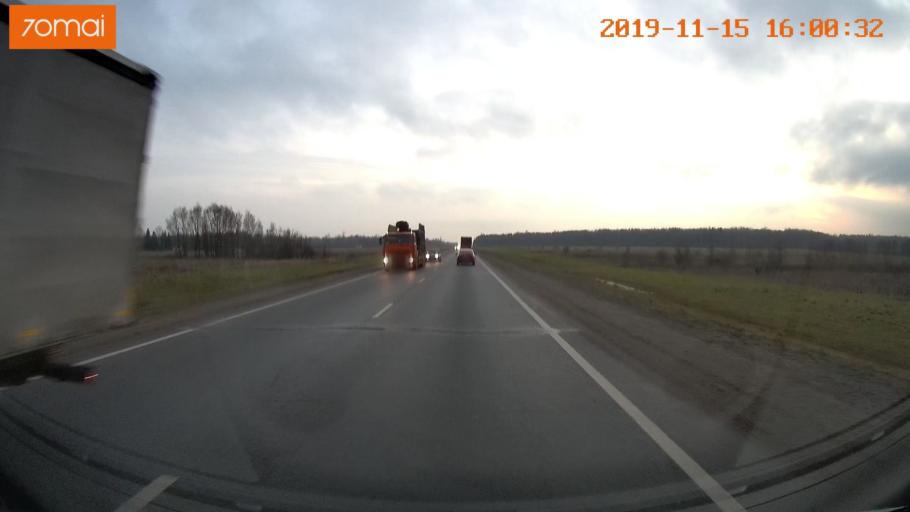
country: RU
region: Jaroslavl
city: Yaroslavl
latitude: 57.7948
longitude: 39.9382
